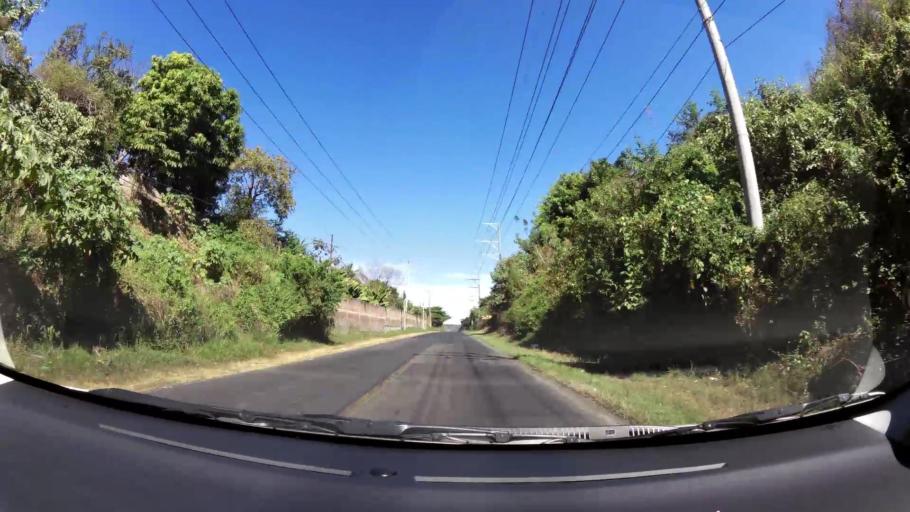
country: SV
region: La Libertad
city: San Juan Opico
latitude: 13.8340
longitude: -89.3586
